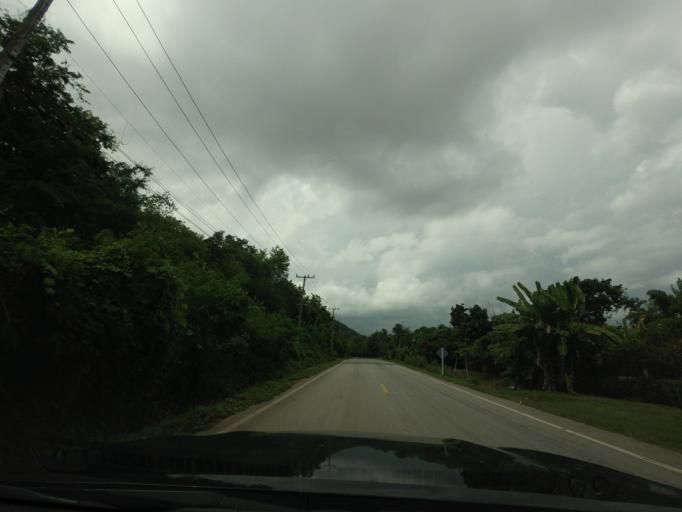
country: TH
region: Loei
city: Pak Chom
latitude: 18.0606
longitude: 101.7982
